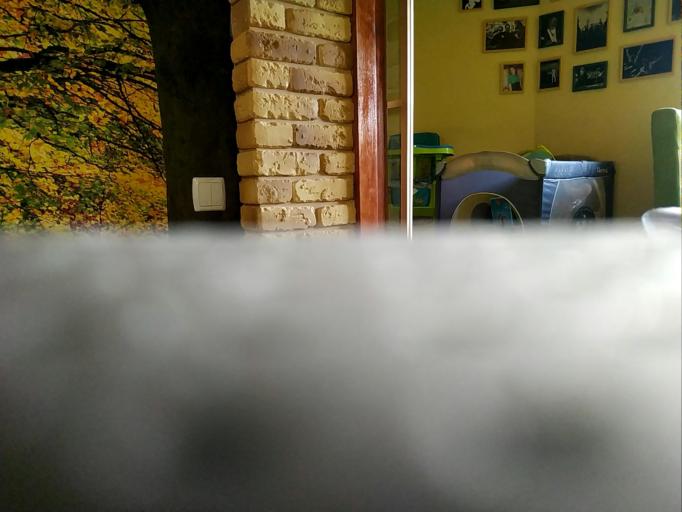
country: RU
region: Kaluga
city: Sukhinichi
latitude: 54.0771
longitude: 35.2882
